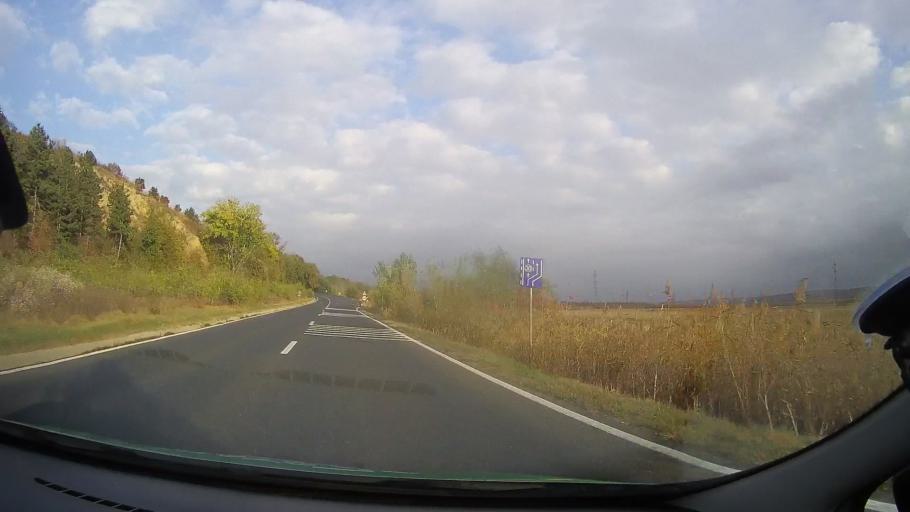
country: RO
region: Constanta
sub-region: Comuna Mircea Voda
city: Mircea Voda
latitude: 44.2692
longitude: 28.1893
